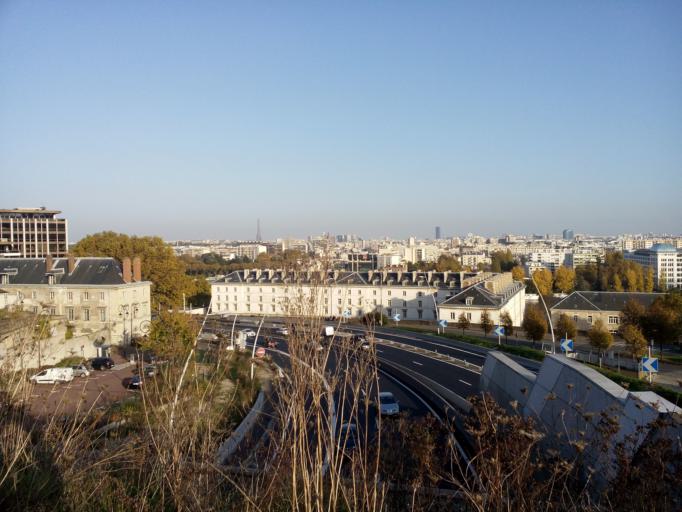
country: FR
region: Ile-de-France
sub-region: Departement des Hauts-de-Seine
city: Saint-Cloud
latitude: 48.8393
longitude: 2.2178
